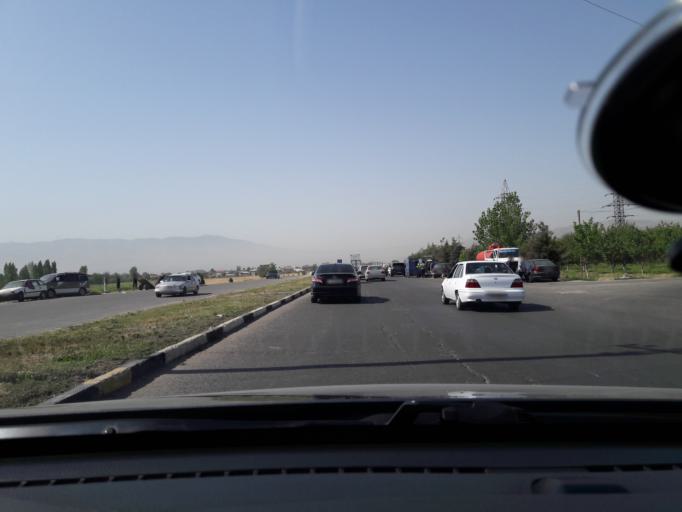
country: TJ
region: Dushanbe
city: Dushanbe
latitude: 38.4992
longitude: 68.7555
